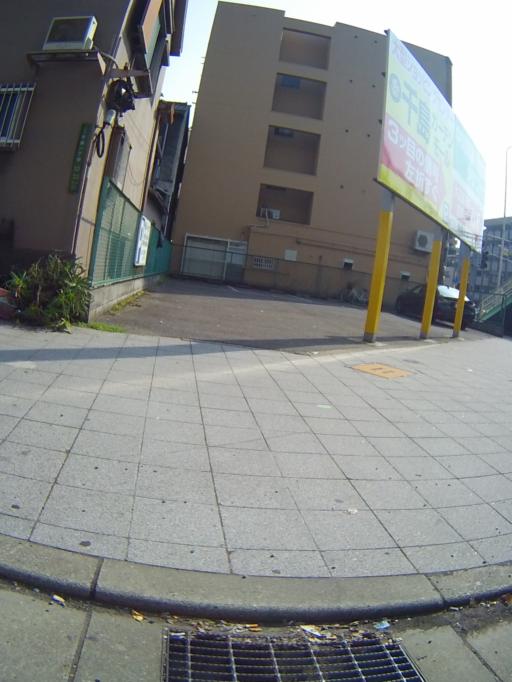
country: JP
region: Osaka
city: Osaka-shi
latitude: 34.6563
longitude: 135.4739
